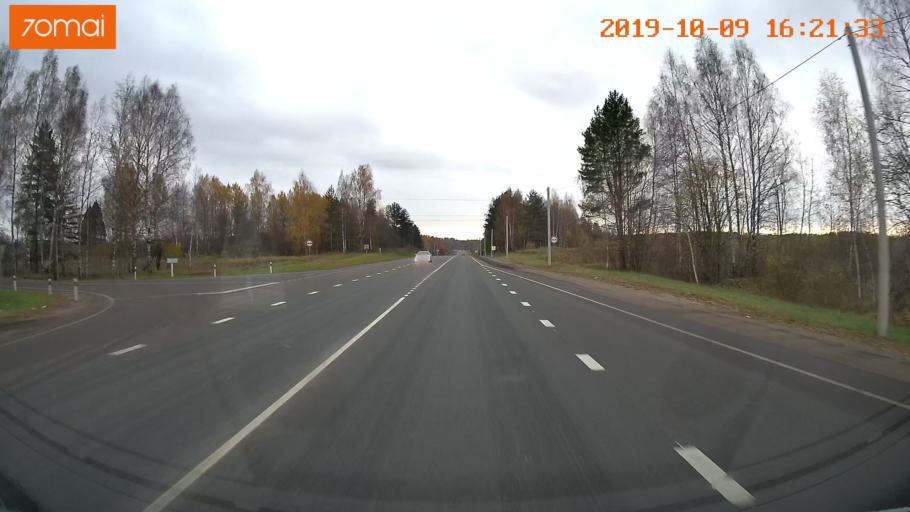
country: RU
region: Kostroma
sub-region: Kostromskoy Rayon
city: Kostroma
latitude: 57.6902
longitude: 40.8888
